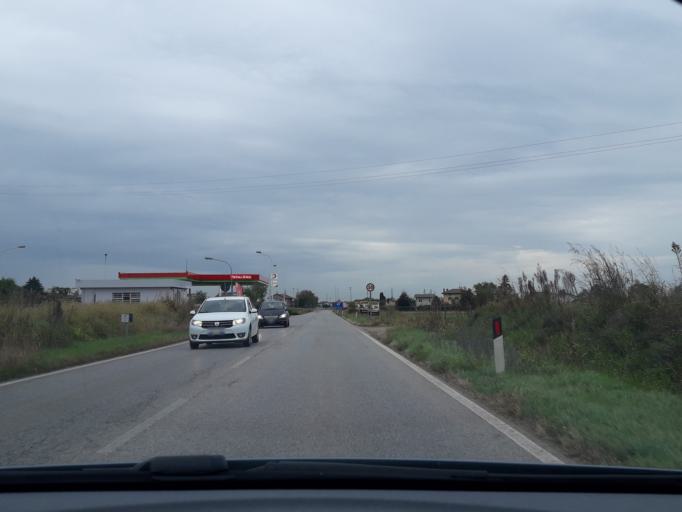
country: IT
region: Friuli Venezia Giulia
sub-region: Provincia di Udine
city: Povoletto
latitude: 46.1056
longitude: 13.2627
